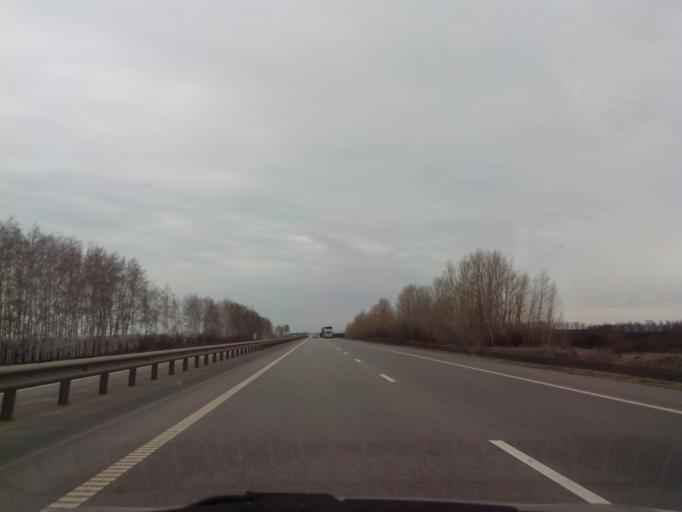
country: RU
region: Tambov
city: Selezni
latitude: 52.8100
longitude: 40.9570
